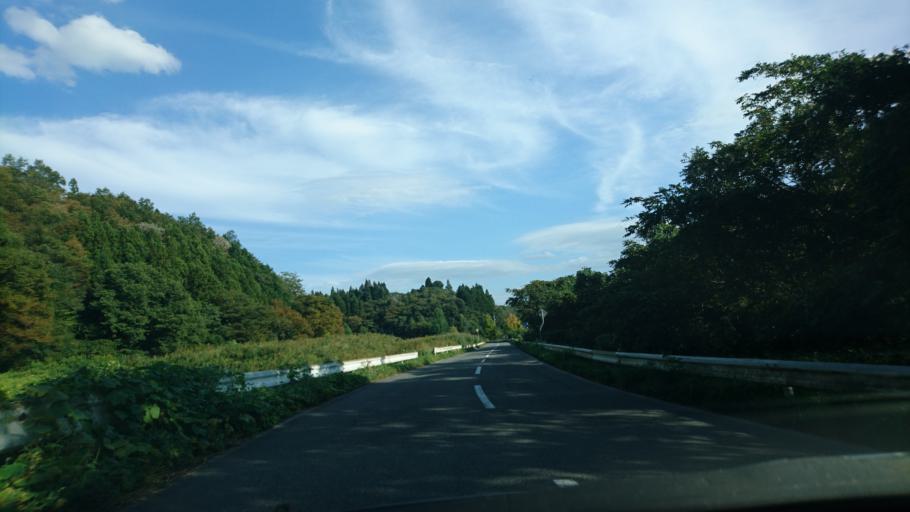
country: JP
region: Iwate
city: Ichinoseki
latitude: 38.8572
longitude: 141.3051
